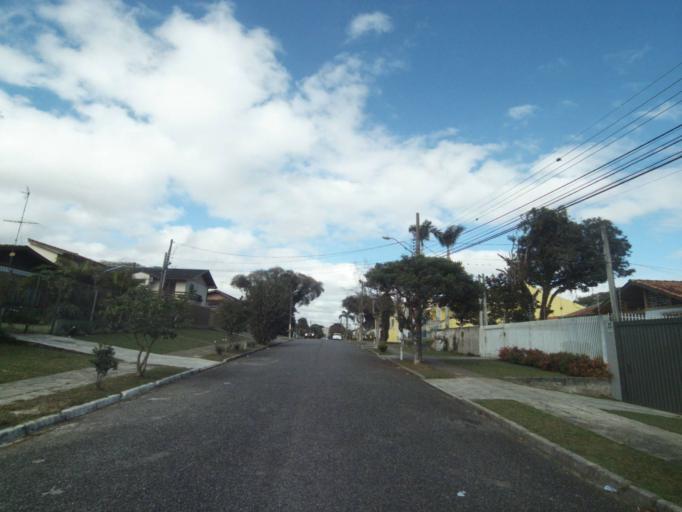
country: BR
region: Parana
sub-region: Curitiba
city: Curitiba
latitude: -25.4597
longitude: -49.2776
